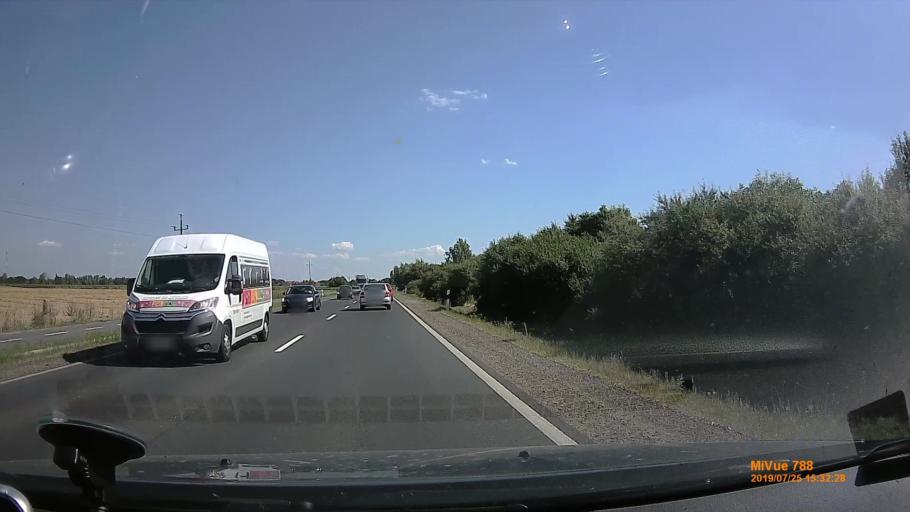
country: HU
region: Borsod-Abauj-Zemplen
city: Malyi
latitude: 48.0061
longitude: 20.8286
